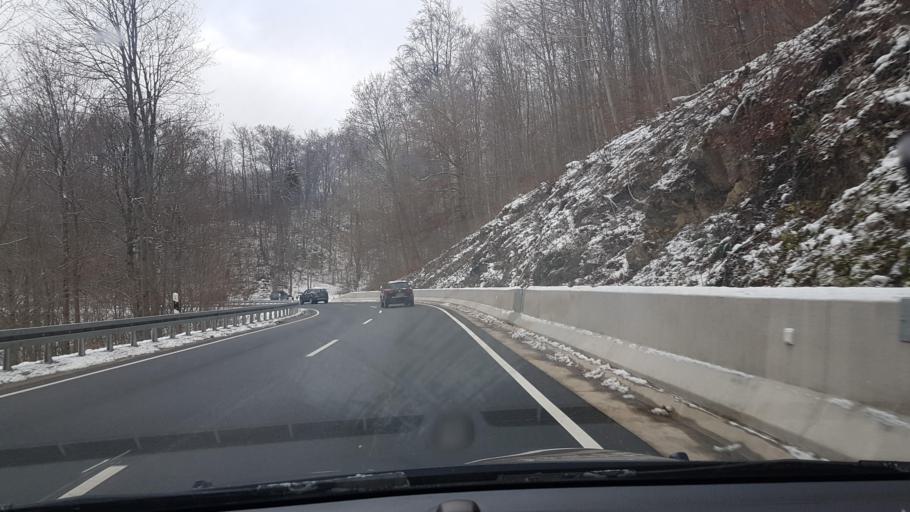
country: DE
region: Lower Saxony
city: Bad Grund
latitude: 51.8196
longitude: 10.2363
